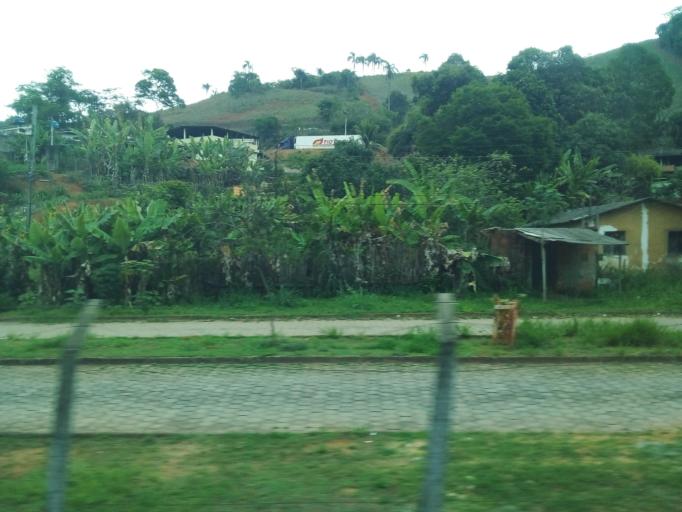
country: BR
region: Minas Gerais
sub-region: Nova Era
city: Nova Era
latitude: -19.7397
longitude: -43.0181
